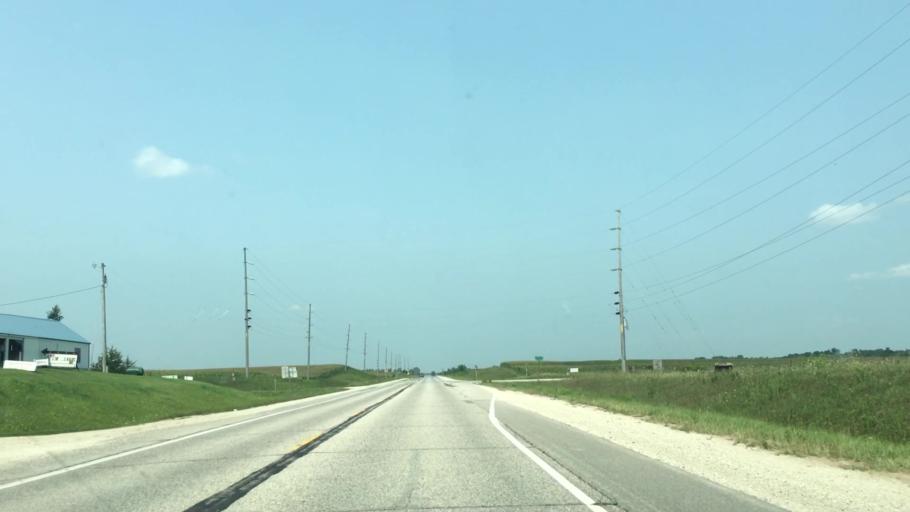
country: US
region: Iowa
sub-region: Fayette County
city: Fayette
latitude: 42.8826
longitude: -91.8105
